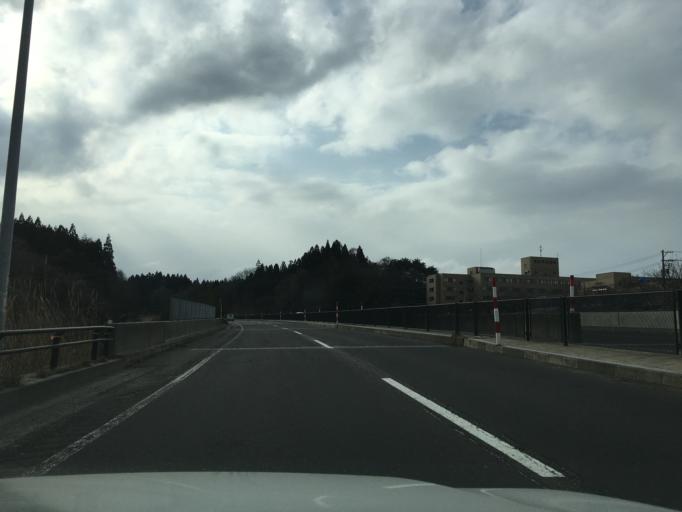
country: JP
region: Aomori
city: Aomori Shi
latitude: 40.8350
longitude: 140.6792
